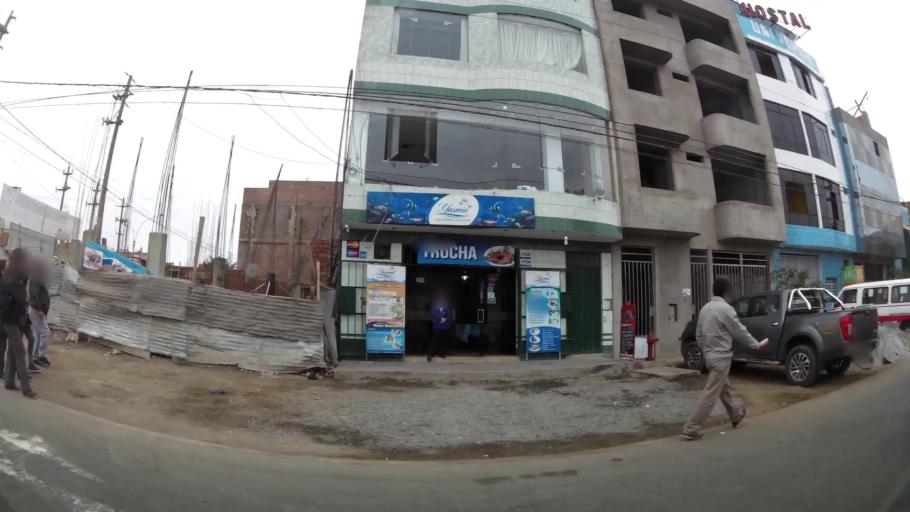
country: PE
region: Lima
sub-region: Lima
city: Carabayllo
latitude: -11.8692
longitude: -77.0738
